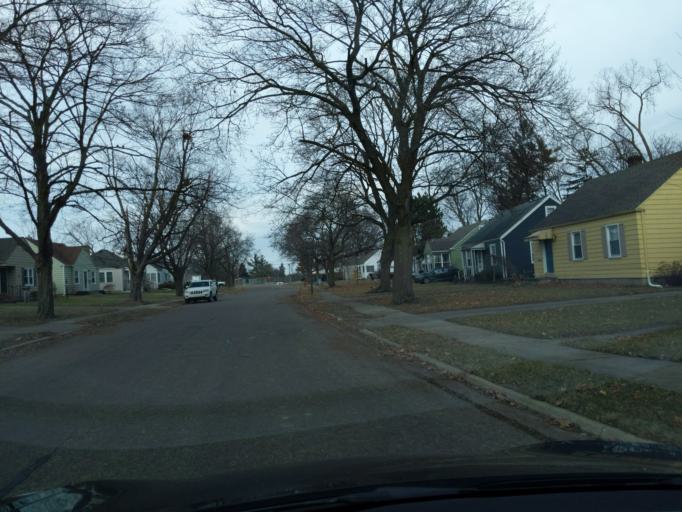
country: US
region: Michigan
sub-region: Ingham County
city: Lansing
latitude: 42.7134
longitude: -84.5739
